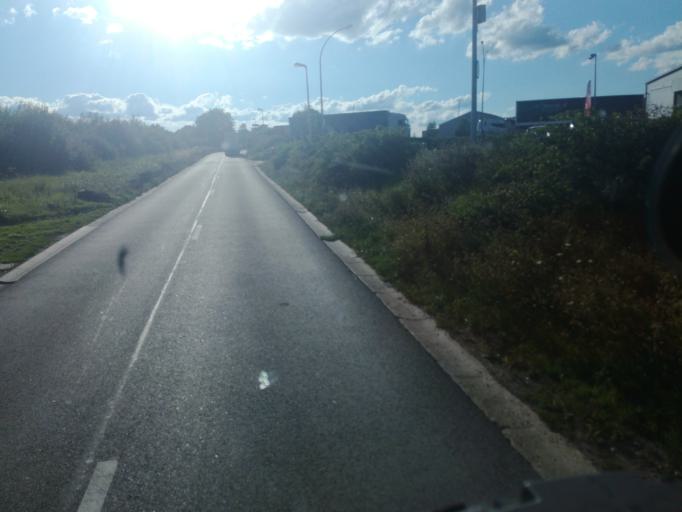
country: BE
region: Wallonia
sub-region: Province du Luxembourg
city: Habay-la-Vieille
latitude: 49.7027
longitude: 5.6253
